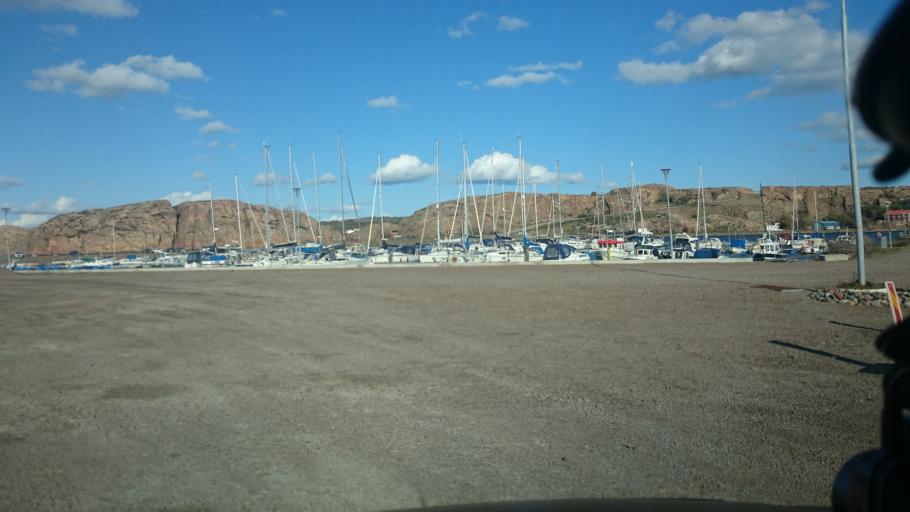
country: SE
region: Vaestra Goetaland
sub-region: Lysekils Kommun
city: Lysekil
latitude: 58.3156
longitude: 11.3951
